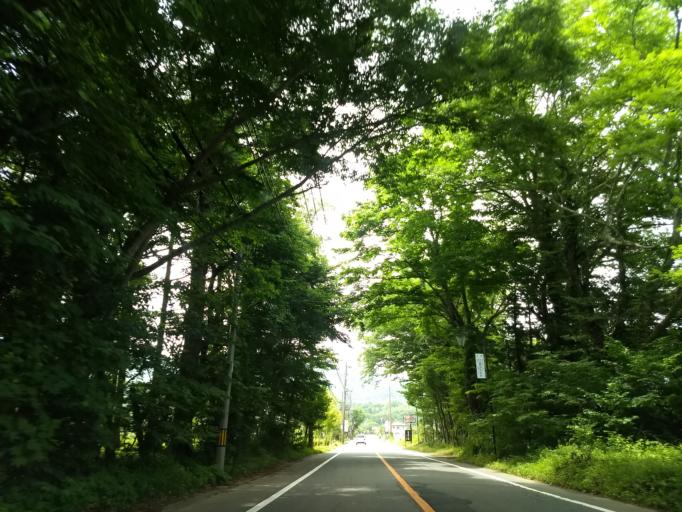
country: JP
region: Shizuoka
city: Gotemba
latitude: 35.4221
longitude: 138.9041
